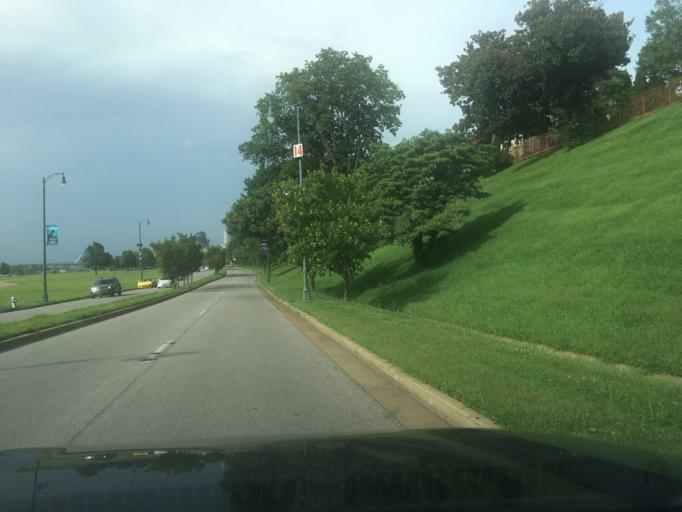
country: US
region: Tennessee
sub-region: Shelby County
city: Memphis
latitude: 35.1325
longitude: -90.0659
